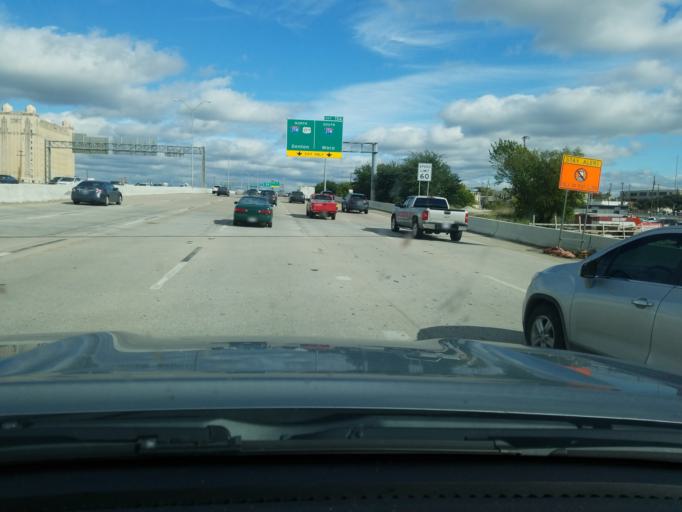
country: US
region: Texas
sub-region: Tarrant County
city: Fort Worth
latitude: 32.7447
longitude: -97.3319
